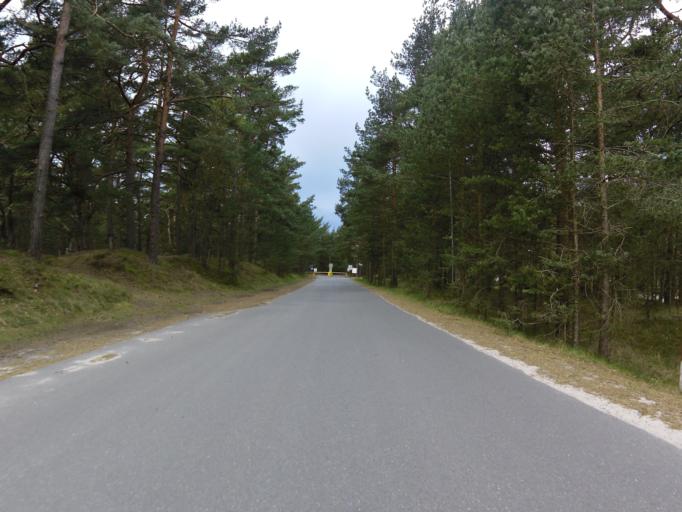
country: DE
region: Mecklenburg-Vorpommern
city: Ostseebad Prerow
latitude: 54.4541
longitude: 12.5479
